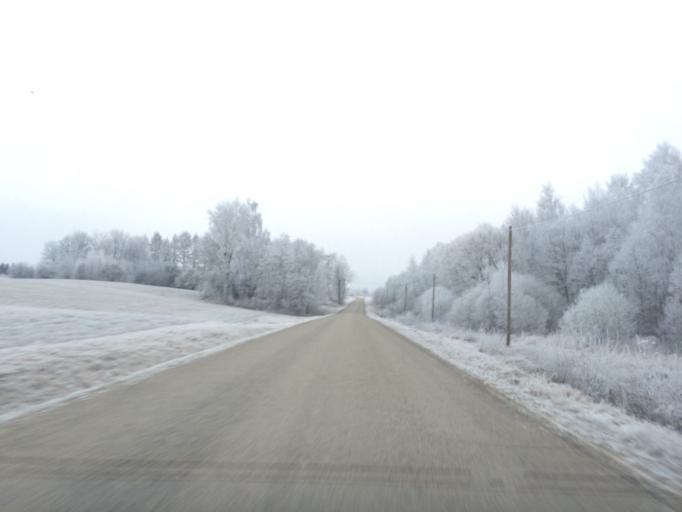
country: LV
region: Ludzas Rajons
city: Ludza
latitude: 56.6366
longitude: 27.5108
